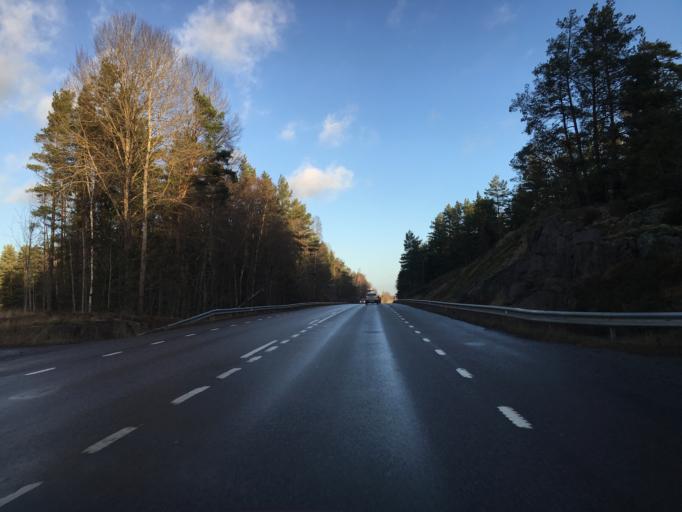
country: SE
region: Kalmar
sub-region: Vasterviks Kommun
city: Ankarsrum
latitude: 57.7042
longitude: 16.4449
